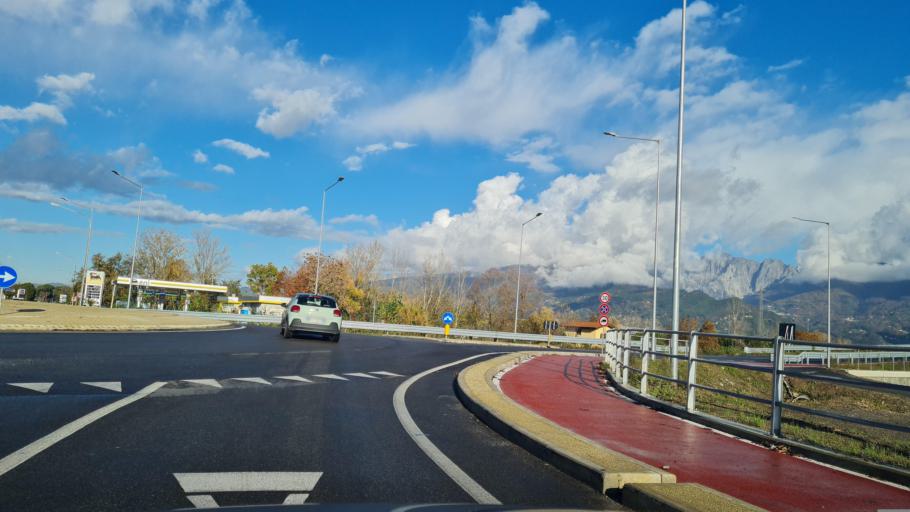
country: IT
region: Tuscany
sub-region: Provincia di Lucca
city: Pietrasanta
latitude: 43.9510
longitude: 10.2020
